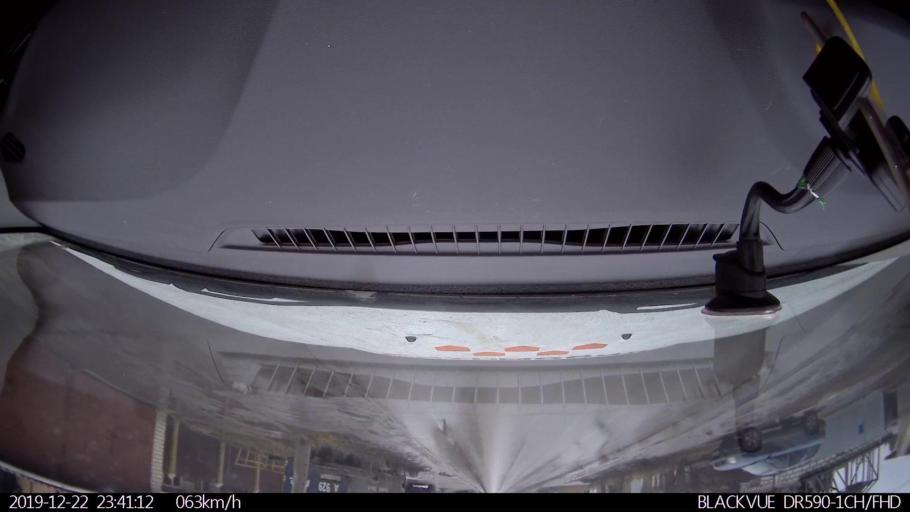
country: RU
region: Nizjnij Novgorod
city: Nizhniy Novgorod
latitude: 56.2833
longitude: 43.9105
